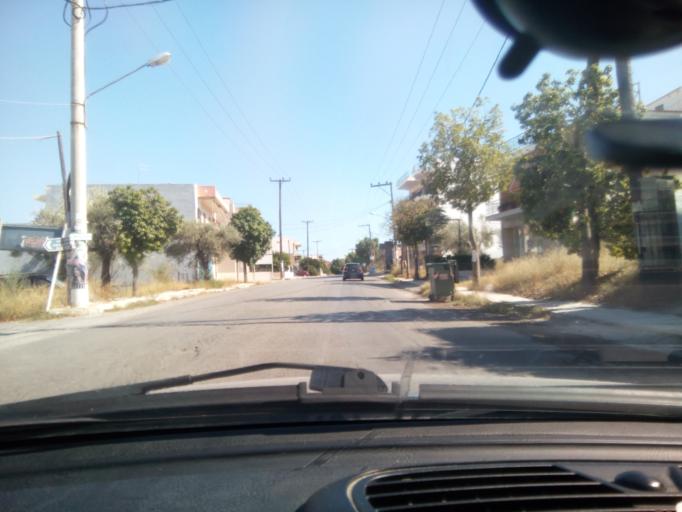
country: GR
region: Central Greece
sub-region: Nomos Evvoias
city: Vasilikon
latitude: 38.4246
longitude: 23.6740
